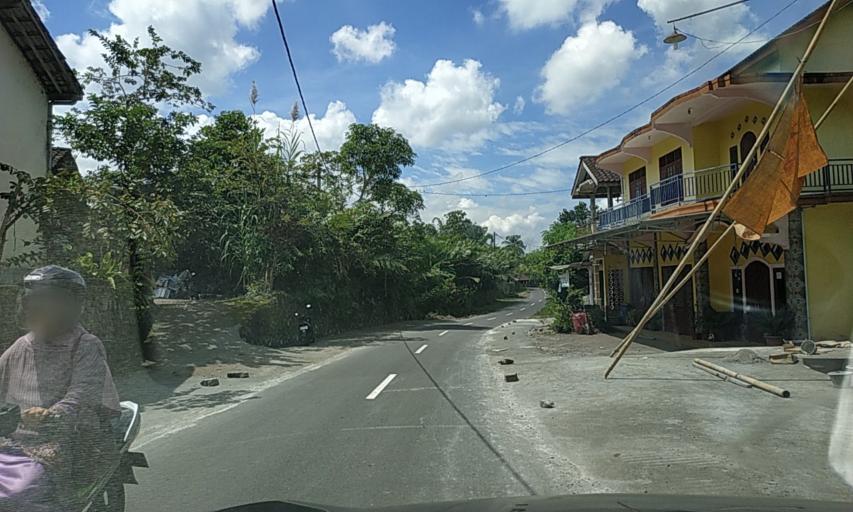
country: ID
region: Daerah Istimewa Yogyakarta
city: Sleman
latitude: -7.6210
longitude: 110.3845
